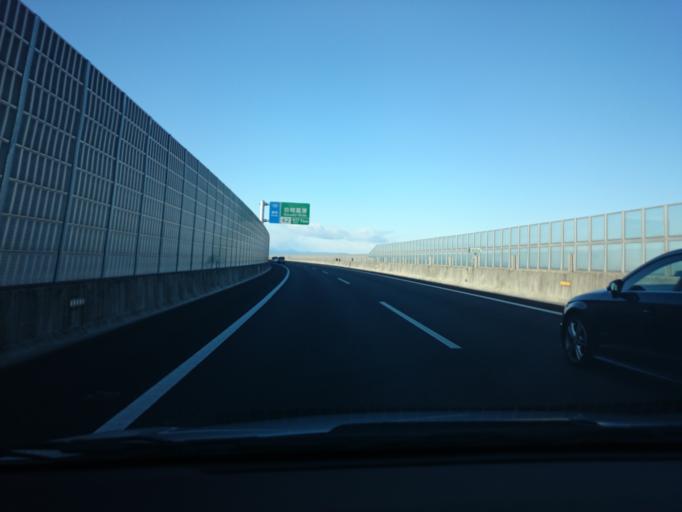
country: JP
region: Saitama
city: Shobu
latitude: 36.0511
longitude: 139.6346
